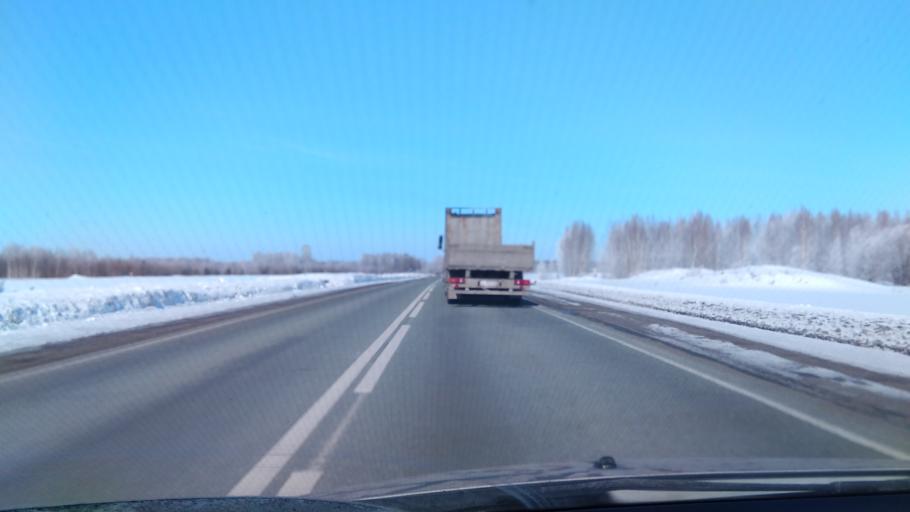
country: RU
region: Perm
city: Suksun
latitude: 56.9358
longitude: 57.5420
